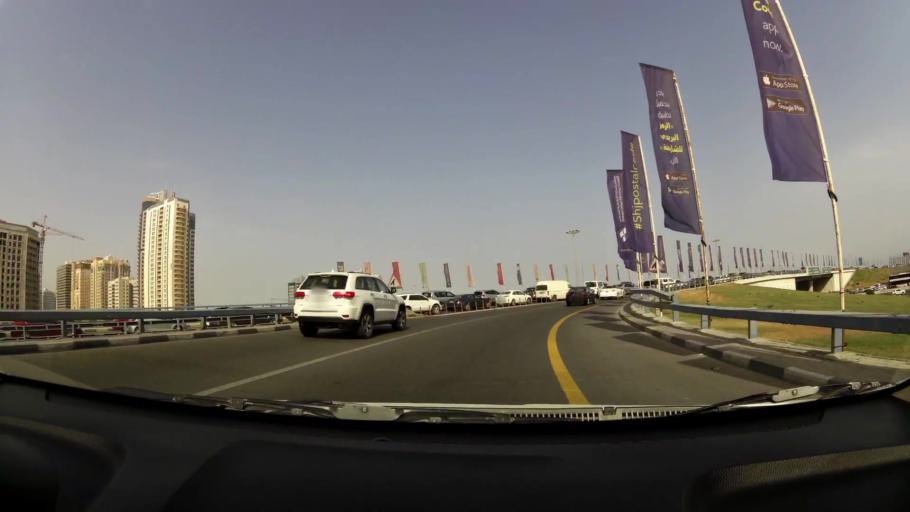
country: AE
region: Ash Shariqah
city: Sharjah
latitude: 25.2997
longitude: 55.3655
